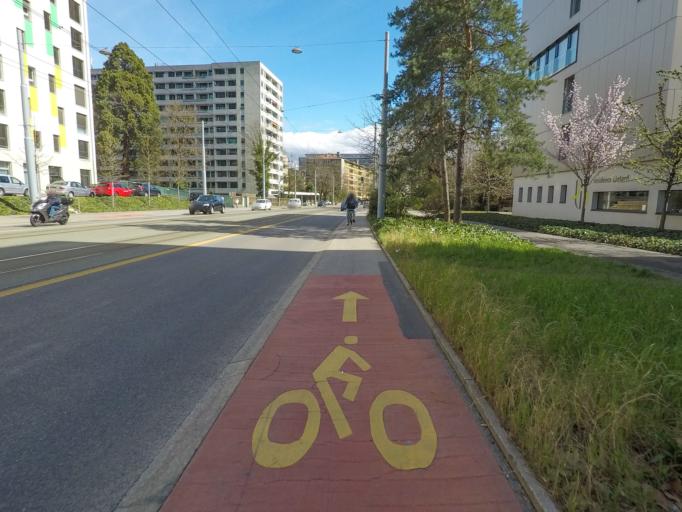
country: CH
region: Geneva
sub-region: Geneva
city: Le Grand-Saconnex
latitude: 46.2148
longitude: 6.1260
